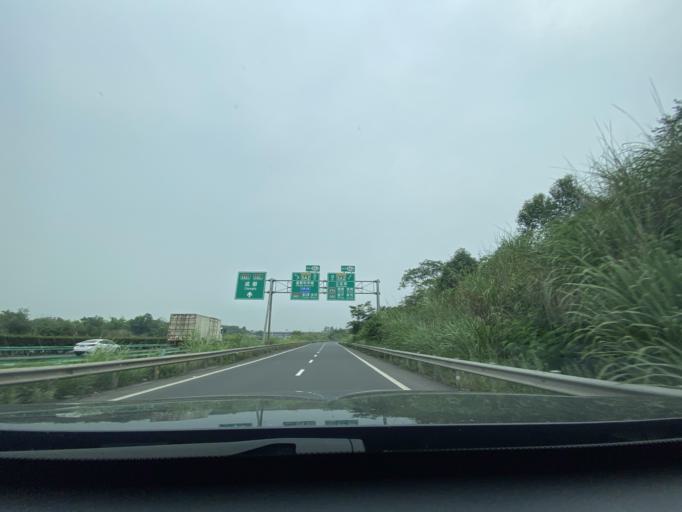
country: CN
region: Sichuan
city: Longquan
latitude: 30.3392
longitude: 104.1185
